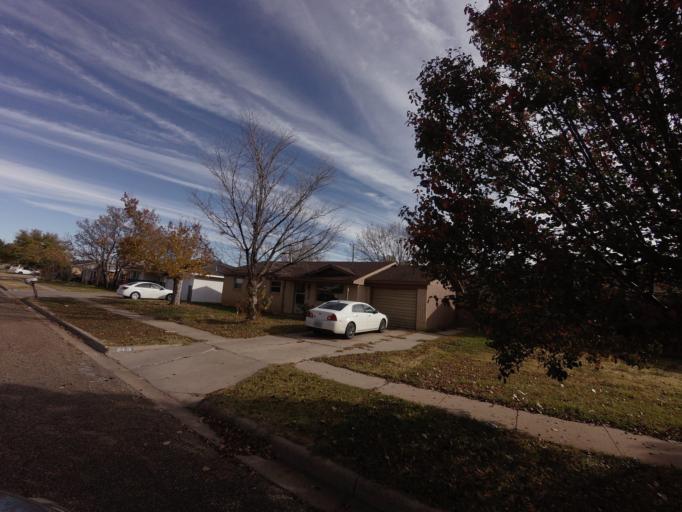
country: US
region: New Mexico
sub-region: Curry County
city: Clovis
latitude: 34.4221
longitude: -103.2234
